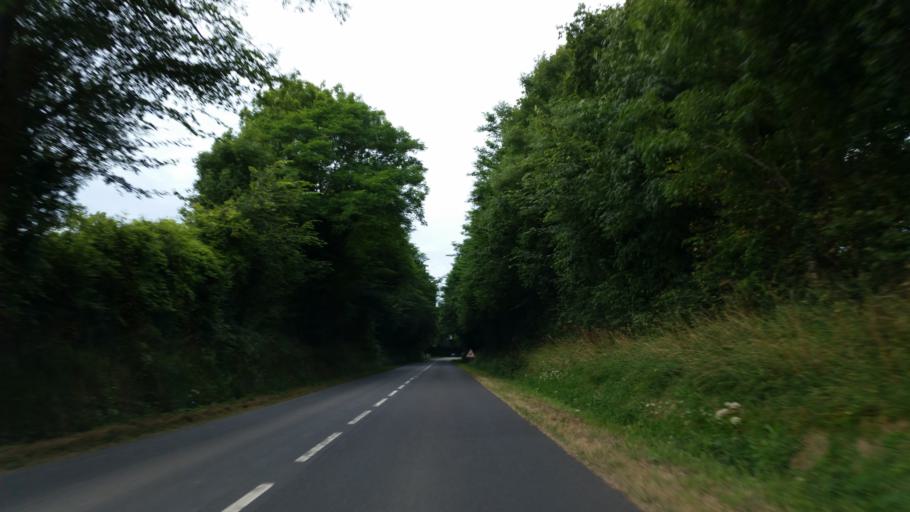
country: FR
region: Lower Normandy
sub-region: Departement du Calvados
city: Le Molay-Littry
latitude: 49.3460
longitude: -0.8908
